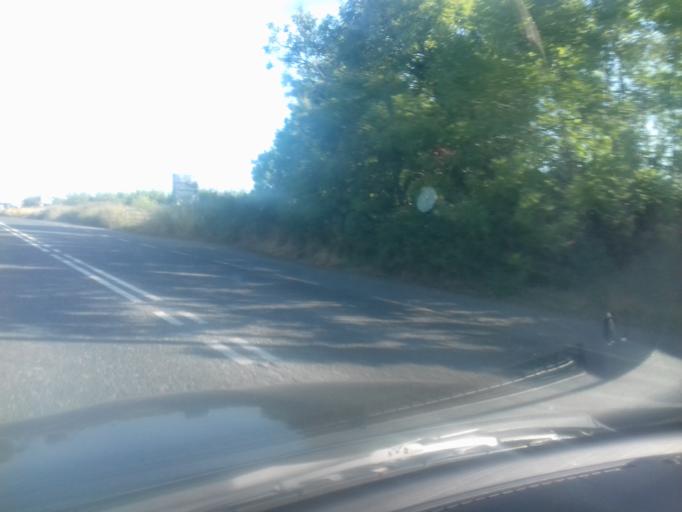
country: IE
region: Leinster
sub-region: An Mhi
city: Ashbourne
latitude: 53.4836
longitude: -6.3728
